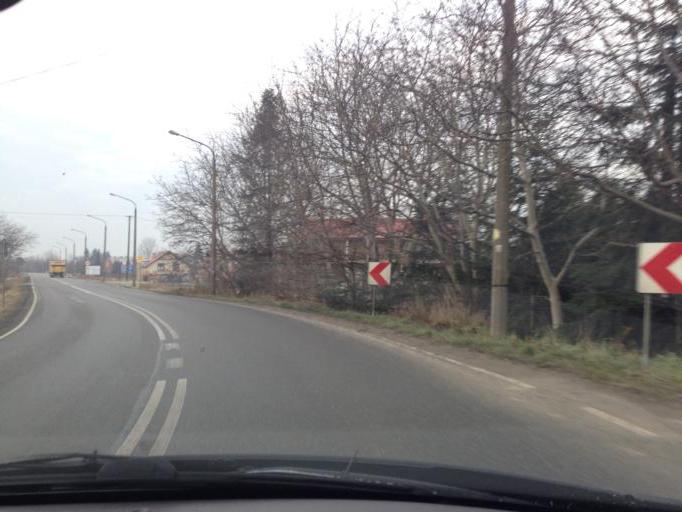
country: PL
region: Lesser Poland Voivodeship
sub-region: Powiat wielicki
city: Kokotow
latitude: 50.0568
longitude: 20.0674
